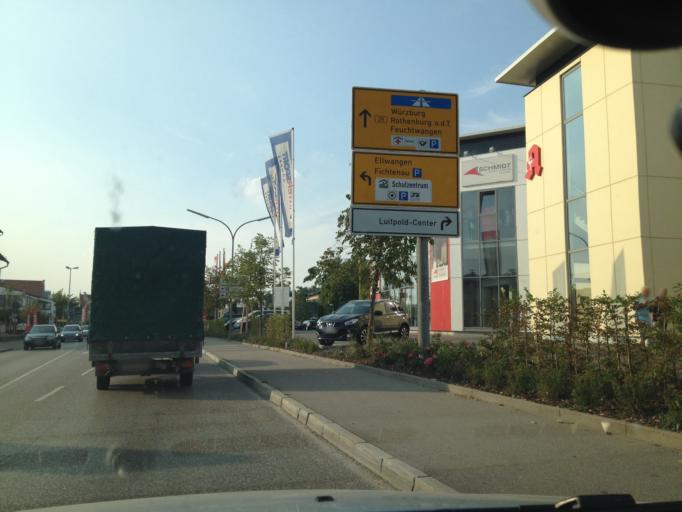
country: DE
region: Bavaria
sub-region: Regierungsbezirk Mittelfranken
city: Dinkelsbuhl
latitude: 49.0668
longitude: 10.3297
